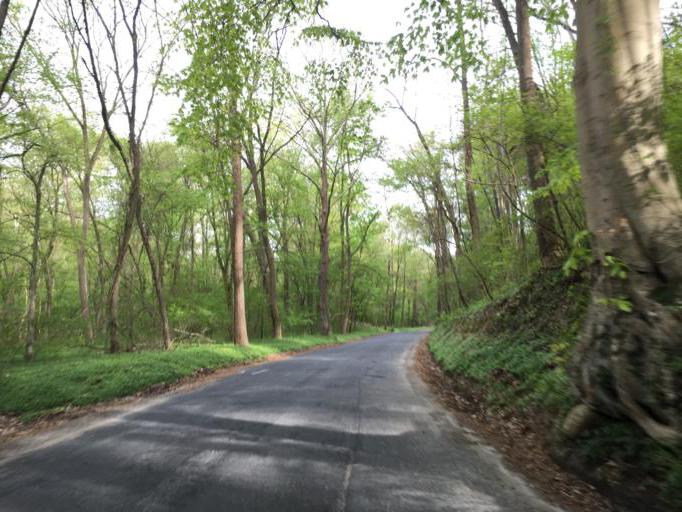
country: US
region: Maryland
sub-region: Howard County
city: Elkridge
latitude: 39.2246
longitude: -76.7176
